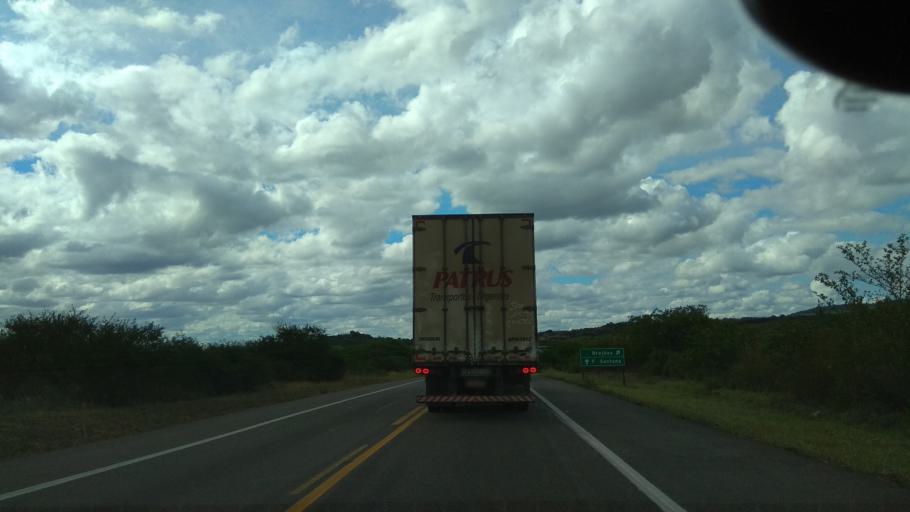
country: BR
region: Bahia
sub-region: Santa Ines
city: Santa Ines
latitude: -12.9864
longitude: -39.9442
